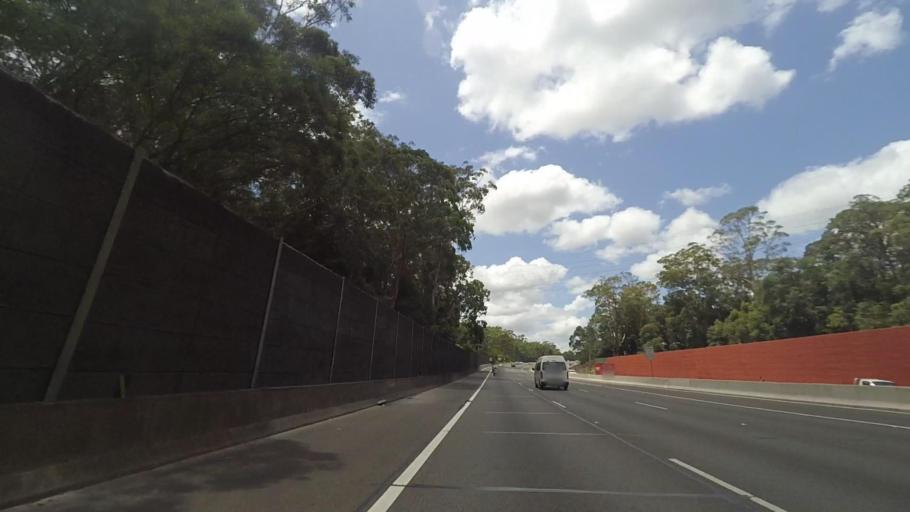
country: AU
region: New South Wales
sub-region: The Hills Shire
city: West Pennant
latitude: -33.7628
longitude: 151.0336
